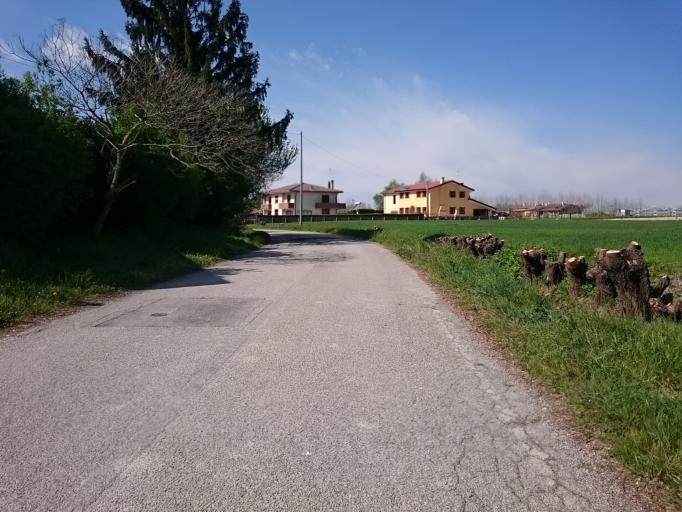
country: IT
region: Veneto
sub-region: Provincia di Padova
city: Polverara
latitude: 45.3081
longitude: 11.9728
